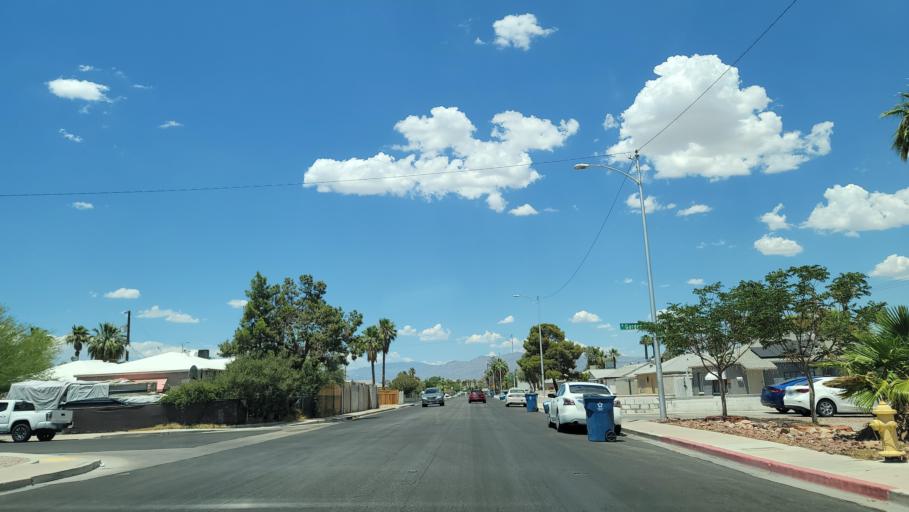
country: US
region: Nevada
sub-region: Clark County
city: Las Vegas
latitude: 36.1637
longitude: -115.1973
